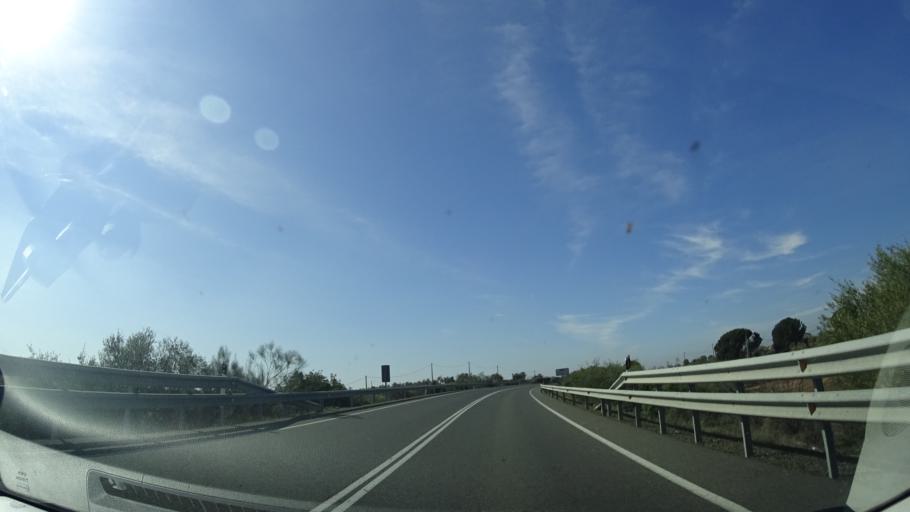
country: ES
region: Andalusia
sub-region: Province of Cordoba
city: Montoro
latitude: 38.0806
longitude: -4.3670
